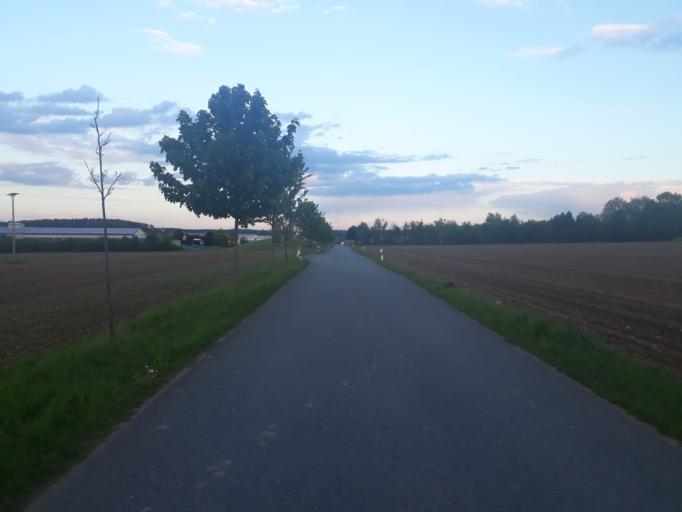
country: DE
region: Saxony
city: Reinhardtsgrimma
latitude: 50.8968
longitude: 13.7515
